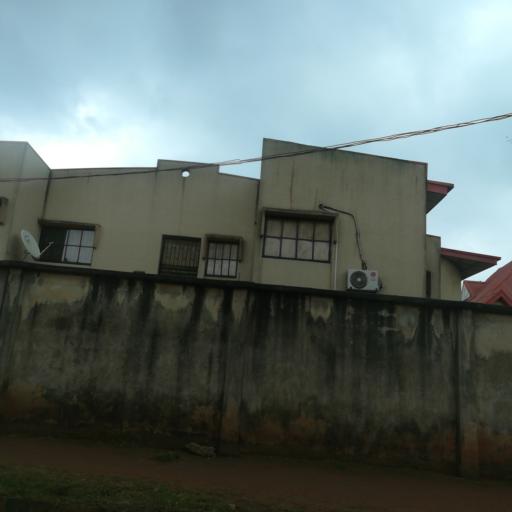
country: NG
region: Lagos
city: Agege
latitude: 6.5934
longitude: 3.3039
